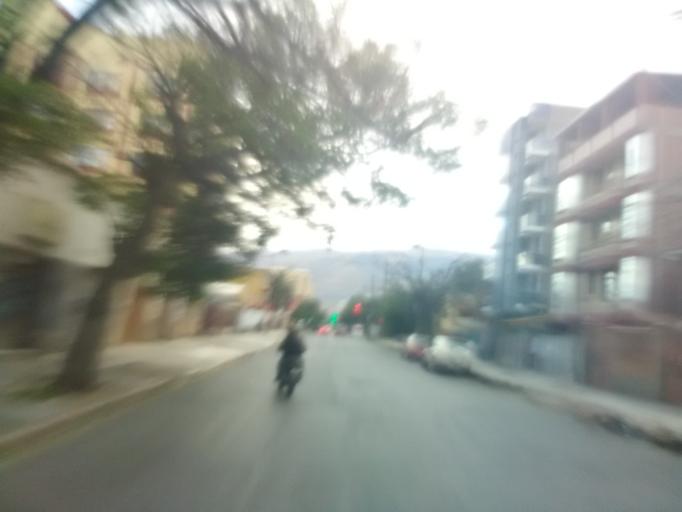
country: BO
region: Cochabamba
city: Cochabamba
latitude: -17.3961
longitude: -66.1490
